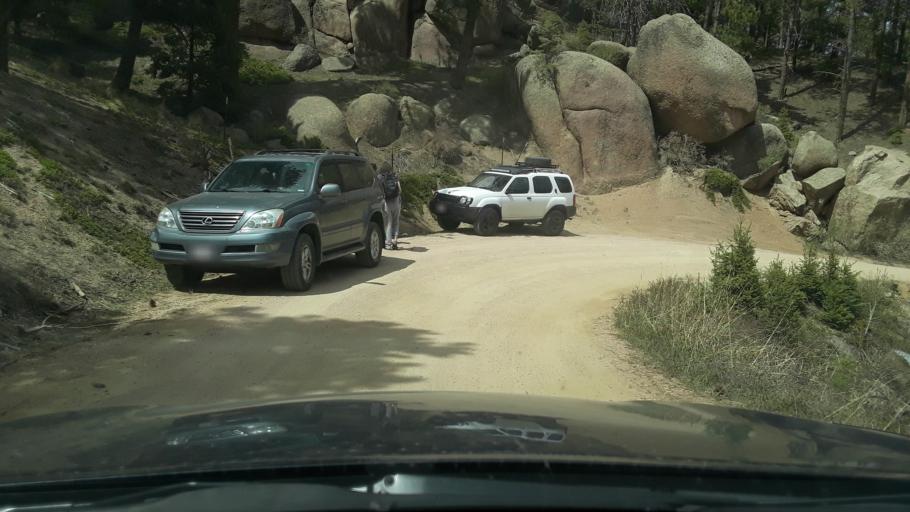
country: US
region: Colorado
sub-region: El Paso County
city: Palmer Lake
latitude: 39.0708
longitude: -104.9418
